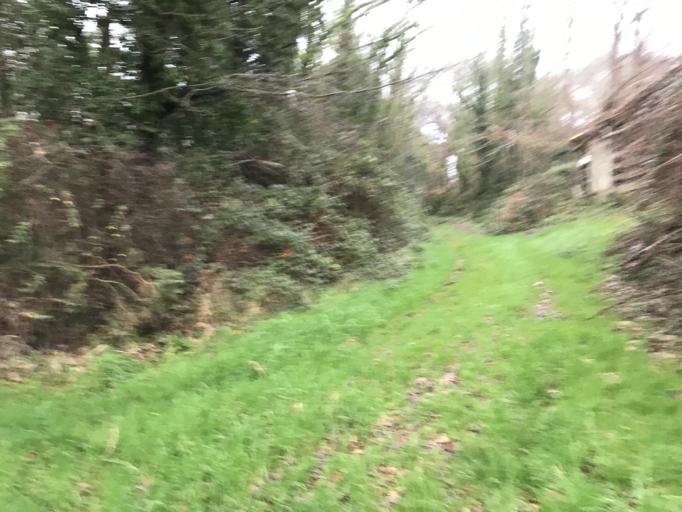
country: FR
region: Brittany
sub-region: Departement du Finistere
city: Logonna-Daoulas
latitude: 48.3245
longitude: -4.2779
